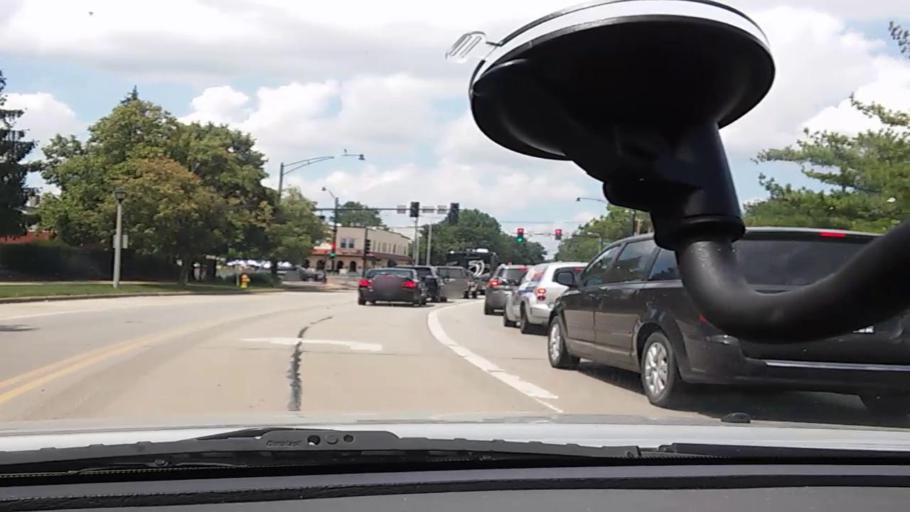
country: US
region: Illinois
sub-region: Peoria County
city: West Peoria
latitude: 40.6990
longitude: -89.6131
